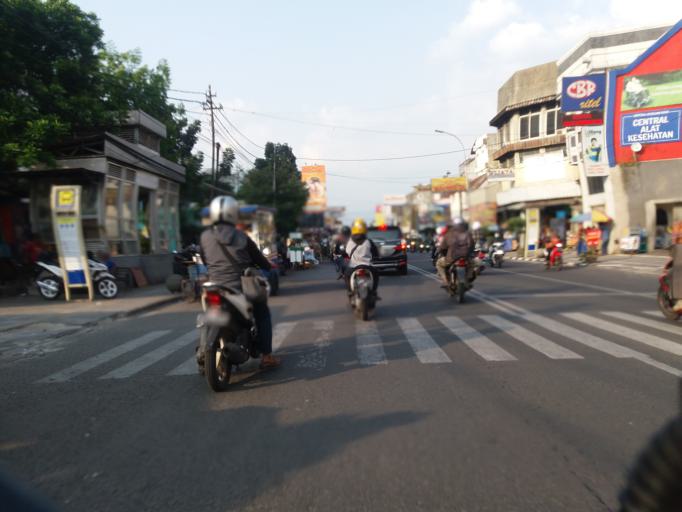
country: ID
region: West Java
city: Bandung
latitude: -6.9200
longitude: 107.6220
